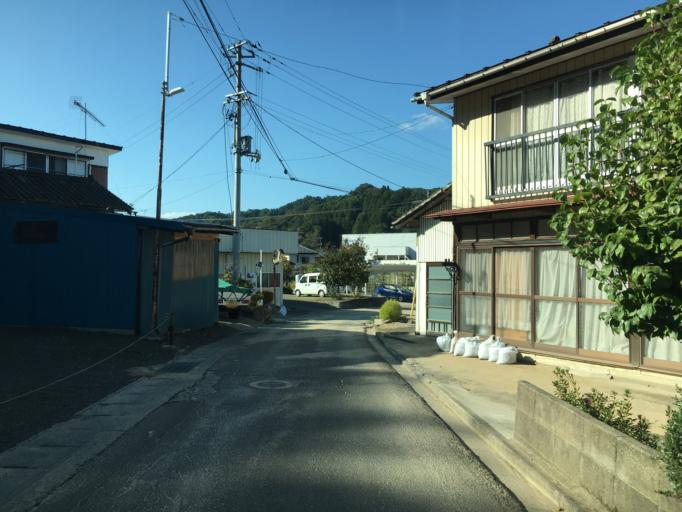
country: JP
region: Fukushima
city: Hobaramachi
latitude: 37.6657
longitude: 140.6087
